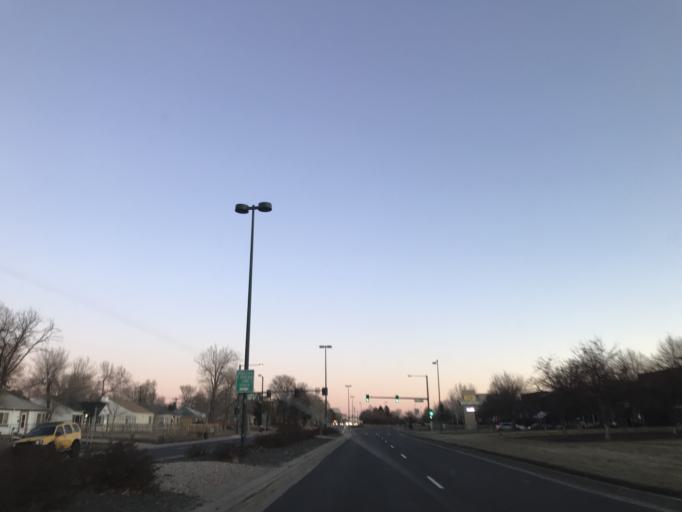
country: US
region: Colorado
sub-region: Adams County
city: Commerce City
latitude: 39.7571
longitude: -104.9034
